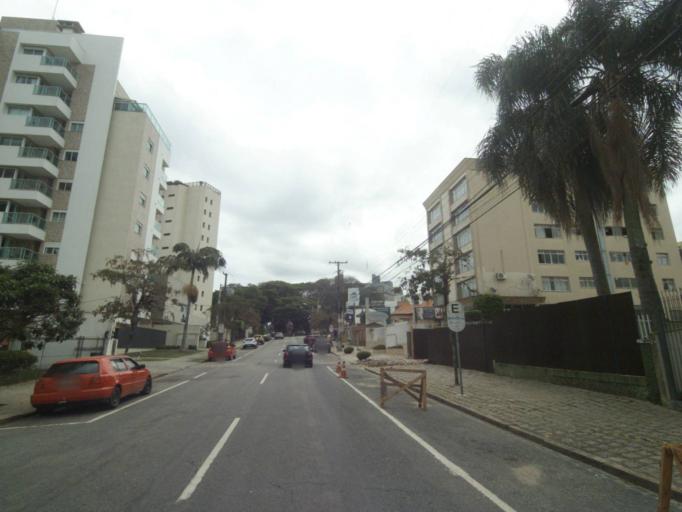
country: BR
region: Parana
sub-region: Curitiba
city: Curitiba
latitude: -25.4339
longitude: -49.2897
